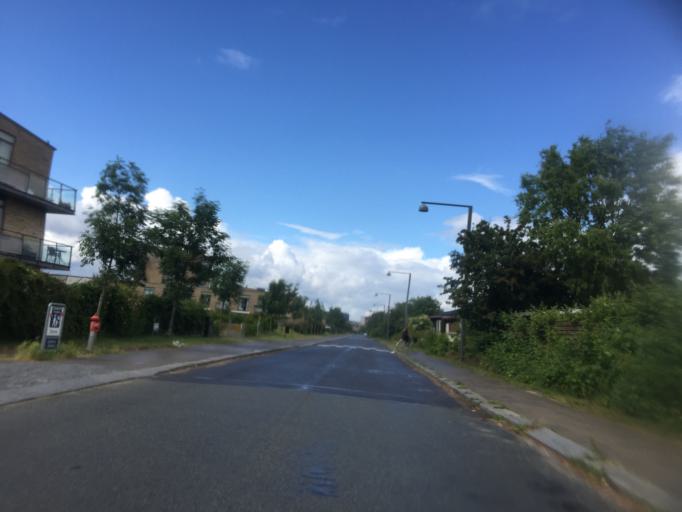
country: DK
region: Capital Region
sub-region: Tarnby Kommune
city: Tarnby
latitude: 55.6451
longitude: 12.5871
